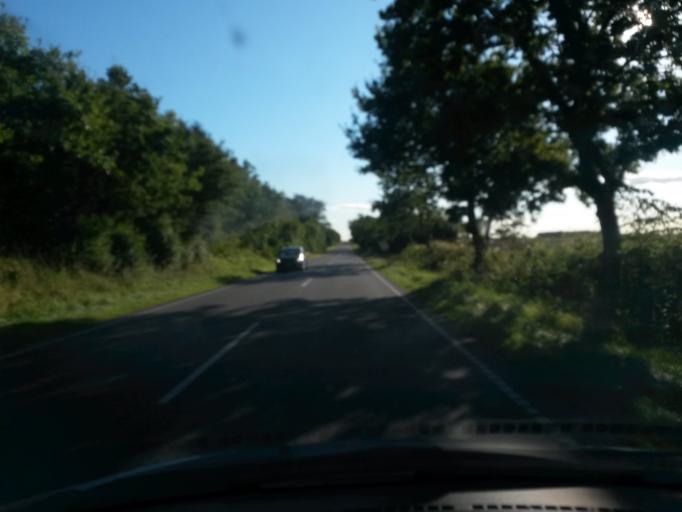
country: DK
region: Central Jutland
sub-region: Silkeborg Kommune
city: Kjellerup
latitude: 56.3090
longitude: 9.5092
